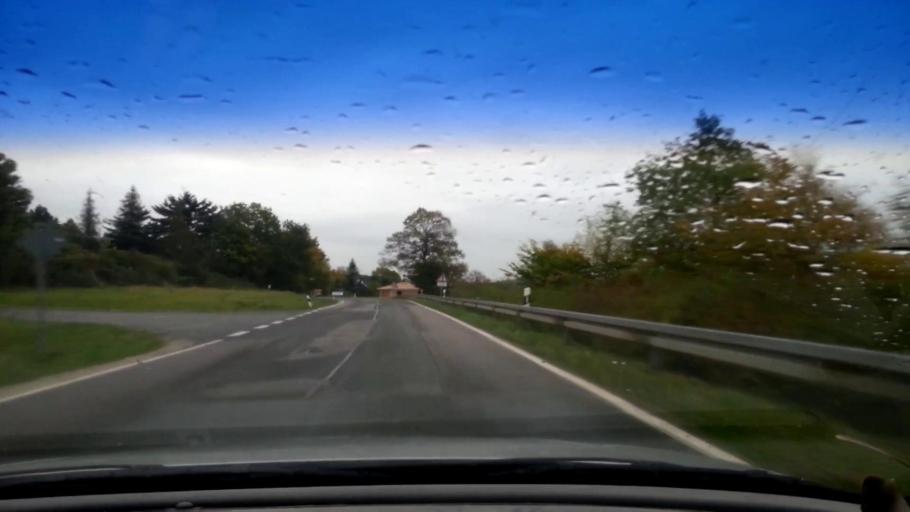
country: DE
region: Bavaria
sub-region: Upper Franconia
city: Priesendorf
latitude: 49.8597
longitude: 10.6836
